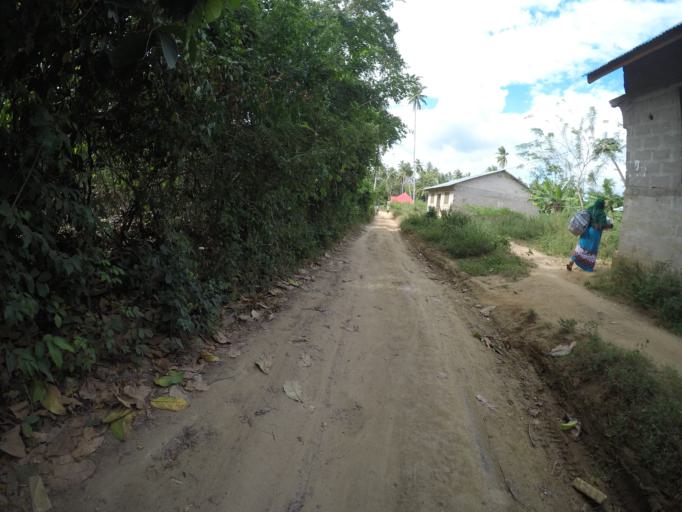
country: TZ
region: Zanzibar Central/South
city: Koani
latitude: -6.1890
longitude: 39.2644
